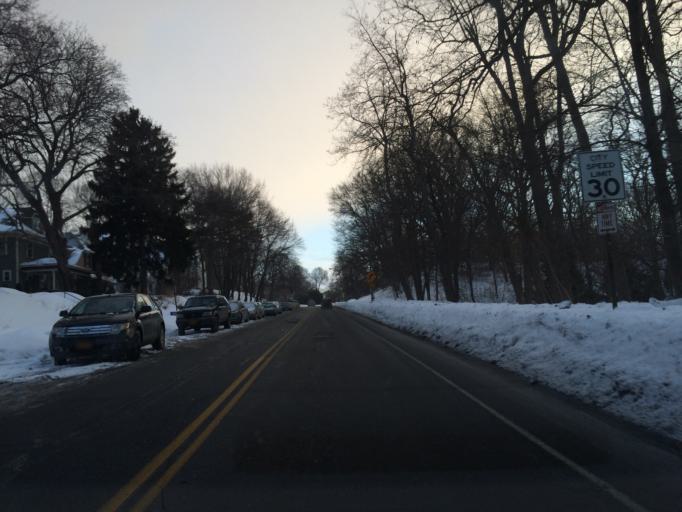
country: US
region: New York
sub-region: Monroe County
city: Rochester
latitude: 43.1349
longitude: -77.6078
